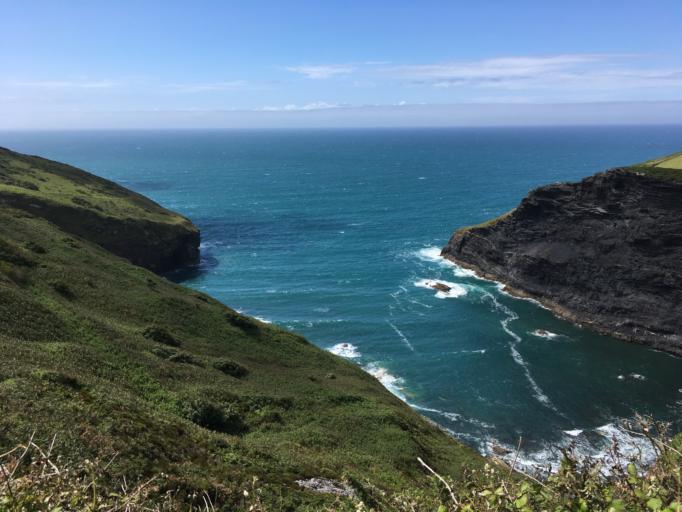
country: GB
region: England
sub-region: Cornwall
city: Camelford
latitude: 50.6950
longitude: -4.6795
